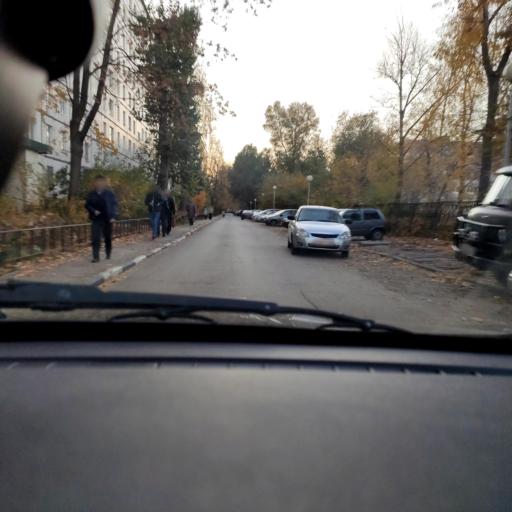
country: RU
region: Samara
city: Tol'yatti
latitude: 53.5367
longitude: 49.2695
